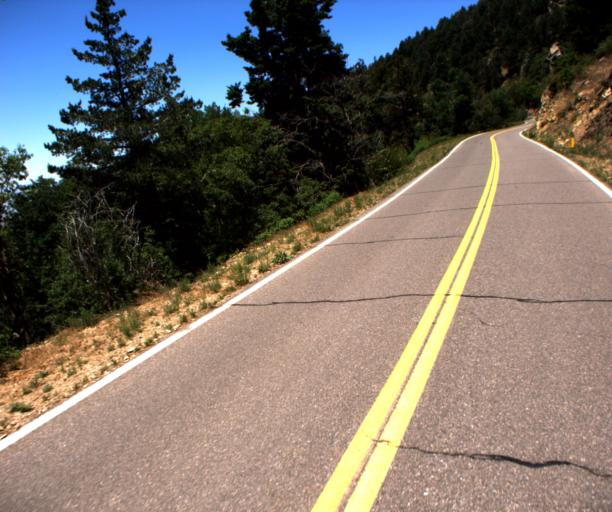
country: US
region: Arizona
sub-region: Graham County
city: Swift Trail Junction
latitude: 32.6466
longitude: -109.8569
